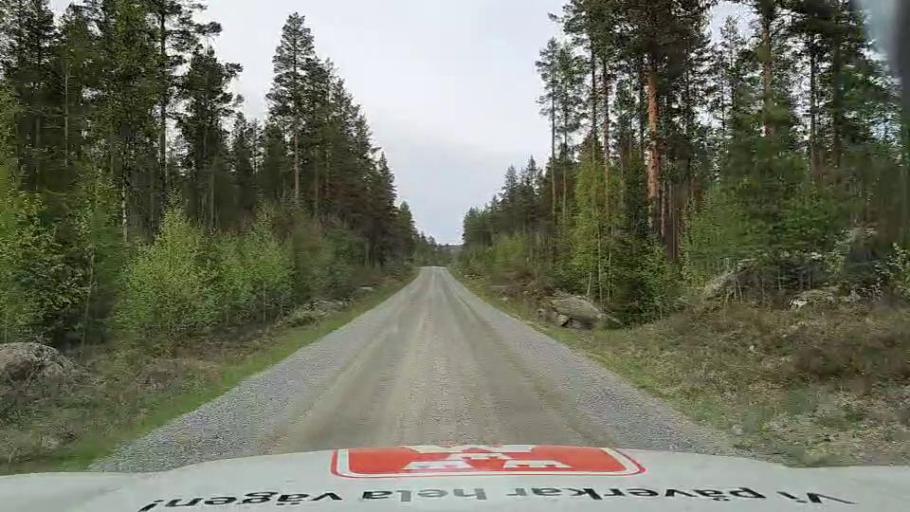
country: SE
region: Jaemtland
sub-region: Braecke Kommun
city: Braecke
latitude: 62.4784
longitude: 14.9171
